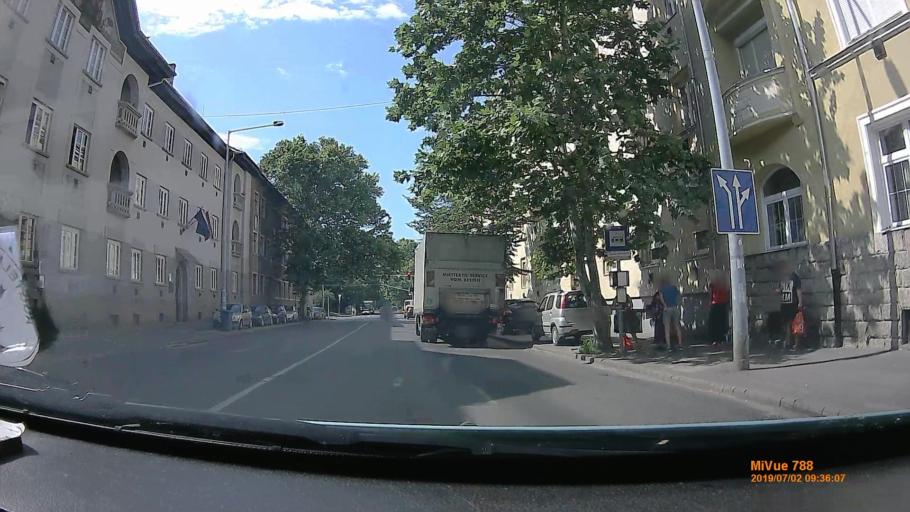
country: HU
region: Borsod-Abauj-Zemplen
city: Miskolc
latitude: 48.1037
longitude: 20.7979
